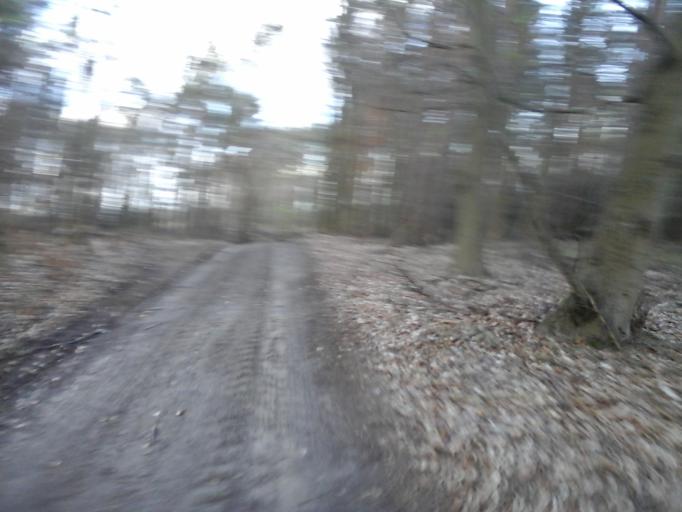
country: PL
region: West Pomeranian Voivodeship
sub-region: Powiat choszczenski
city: Bierzwnik
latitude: 53.0083
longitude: 15.6666
